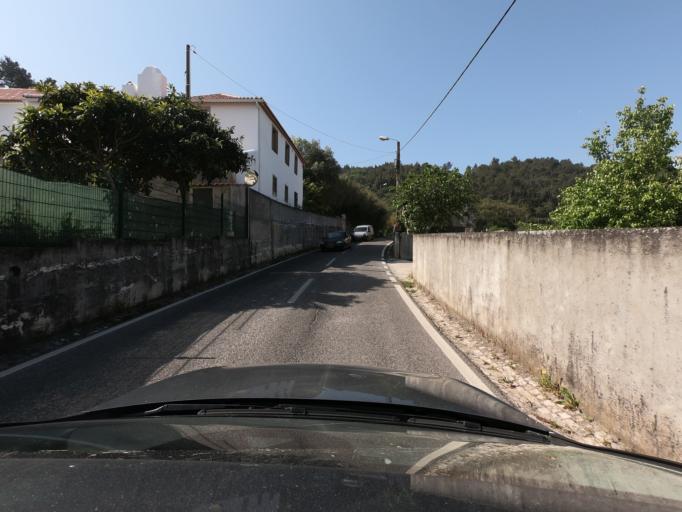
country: PT
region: Lisbon
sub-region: Sintra
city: Sintra
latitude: 38.8045
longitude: -9.3967
